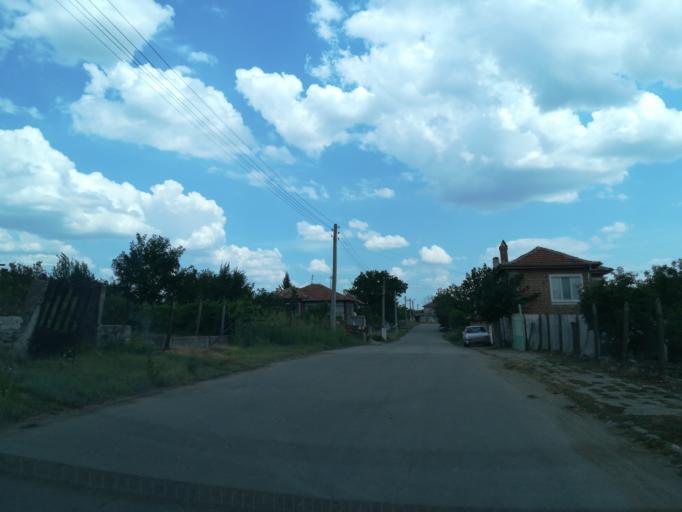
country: BG
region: Khaskovo
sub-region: Obshtina Mineralni Bani
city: Mineralni Bani
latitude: 41.9833
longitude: 25.1689
